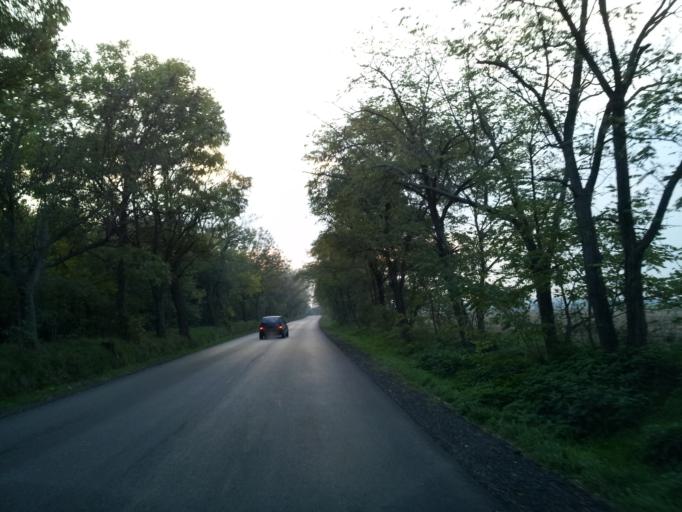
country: HU
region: Gyor-Moson-Sopron
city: Bakonyszentlaszlo
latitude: 47.4666
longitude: 17.8932
